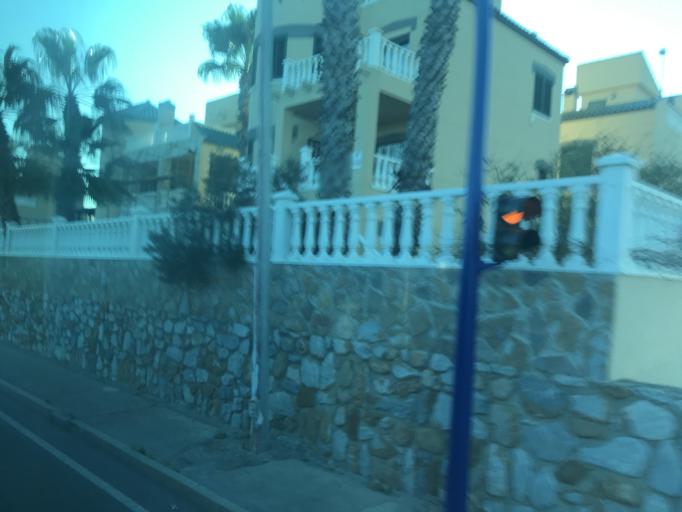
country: ES
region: Valencia
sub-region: Provincia de Alicante
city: Torrevieja
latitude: 38.0006
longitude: -0.6519
